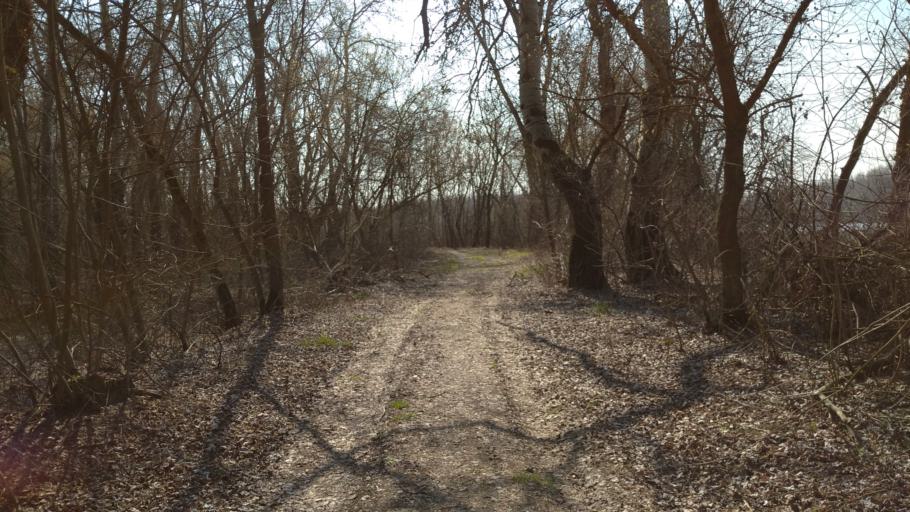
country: HU
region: Csongrad
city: Mindszent
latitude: 46.4847
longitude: 20.2181
